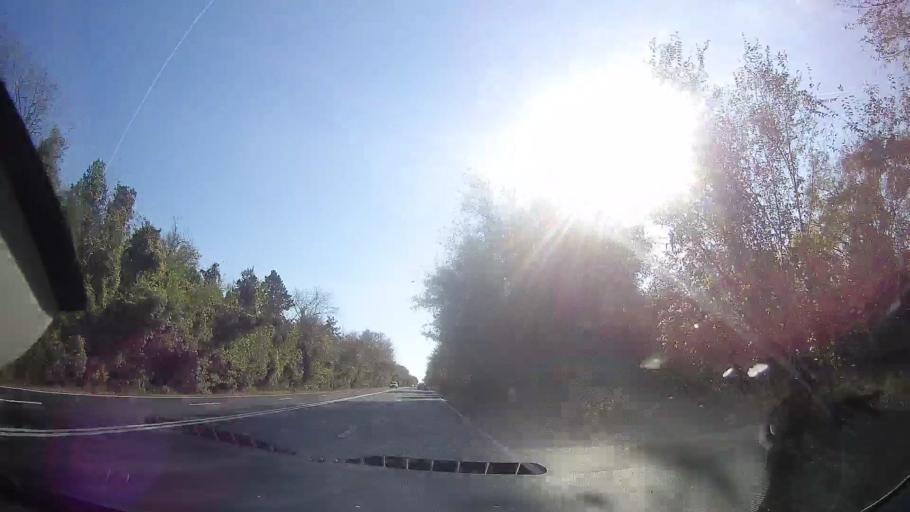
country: RO
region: Constanta
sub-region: Comuna Douazeci si Trei August
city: Dulcesti
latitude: 43.8672
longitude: 28.5748
